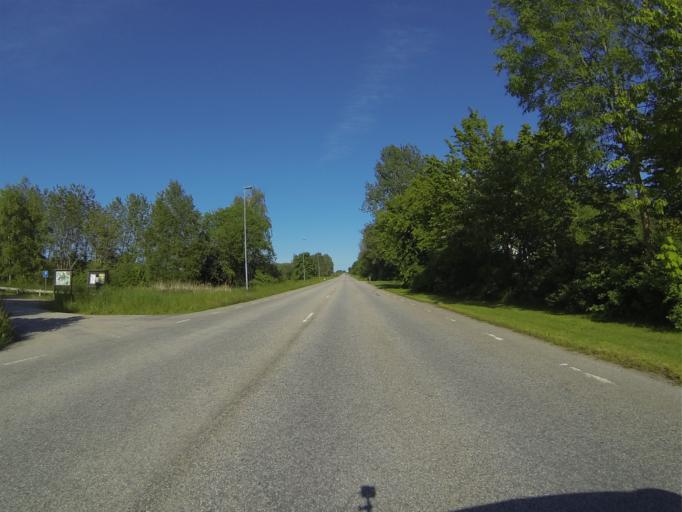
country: SE
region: Skane
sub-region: Lunds Kommun
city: Genarp
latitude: 55.6672
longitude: 13.3702
